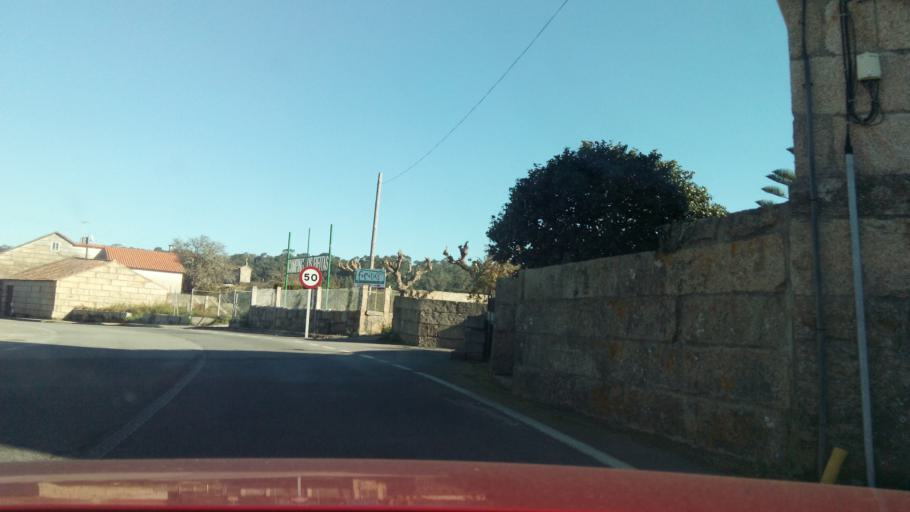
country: ES
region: Galicia
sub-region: Provincia de Pontevedra
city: O Grove
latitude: 42.4683
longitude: -8.9037
